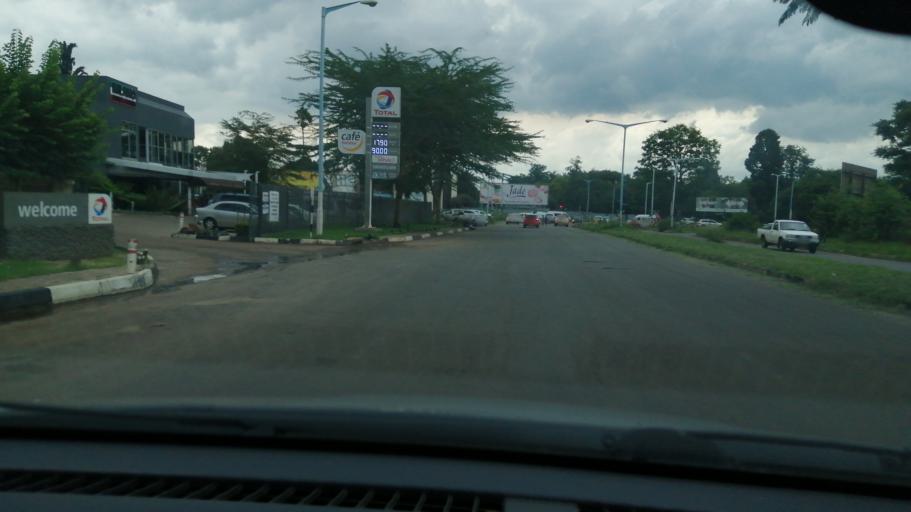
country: ZW
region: Harare
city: Harare
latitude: -17.7914
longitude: 31.0448
